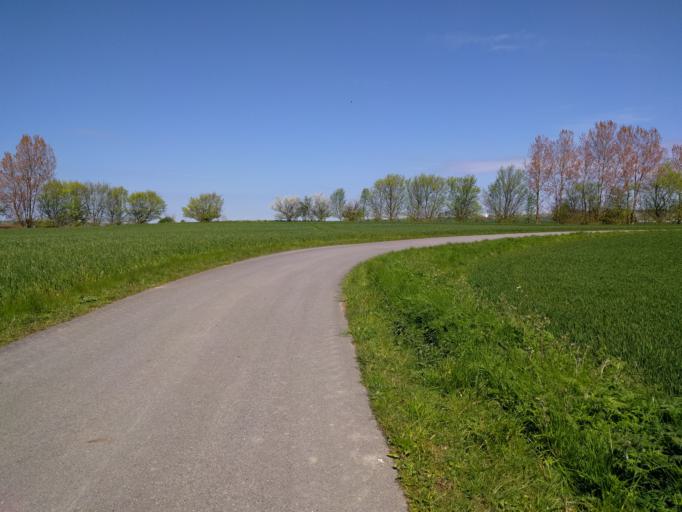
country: DK
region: South Denmark
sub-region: Kerteminde Kommune
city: Munkebo
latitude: 55.4480
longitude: 10.5966
